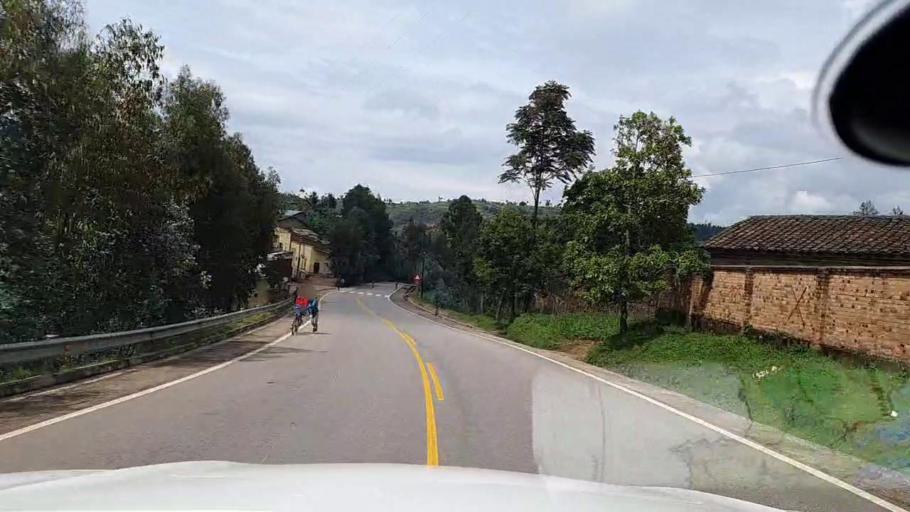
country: RW
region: Southern Province
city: Nzega
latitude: -2.5041
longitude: 29.5084
